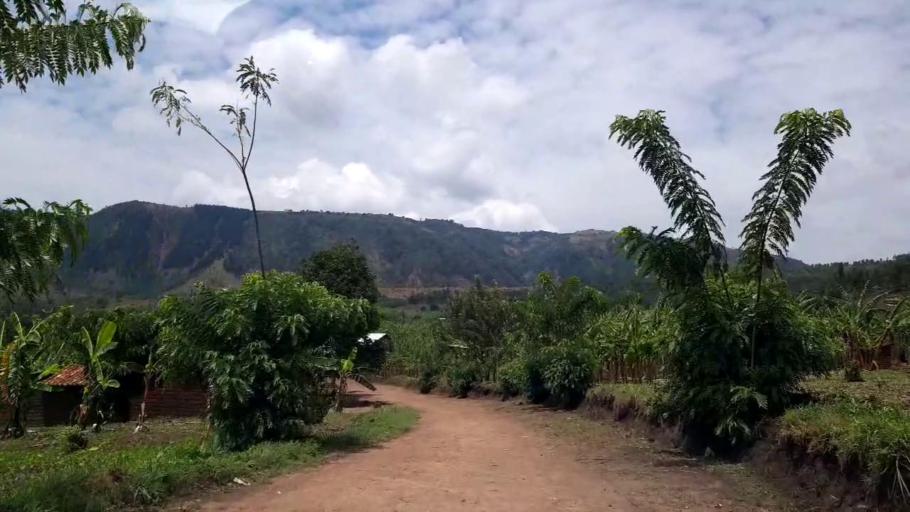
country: RW
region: Northern Province
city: Byumba
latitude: -1.4904
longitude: 30.1998
